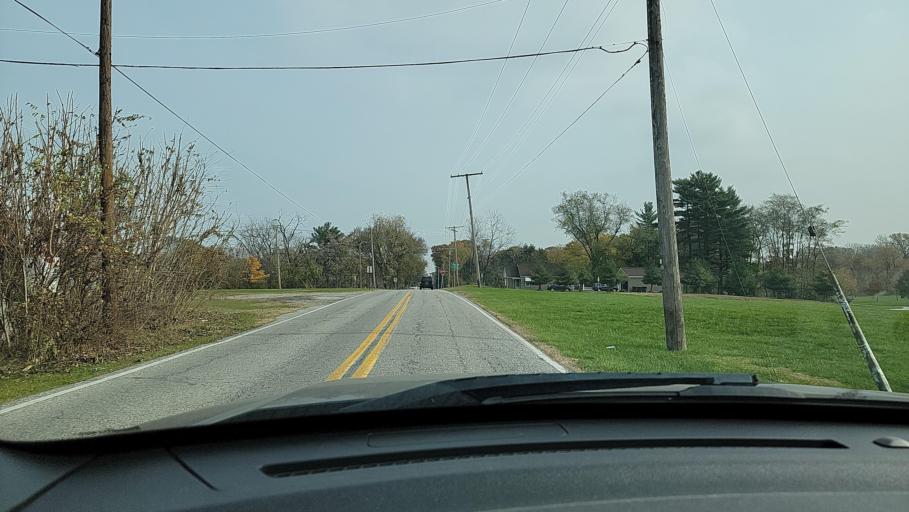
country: US
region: Indiana
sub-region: Porter County
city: Portage
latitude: 41.5868
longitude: -87.1748
